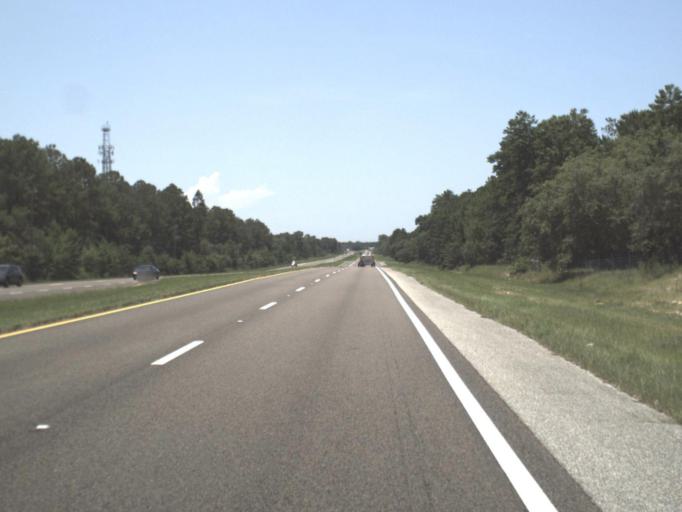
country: US
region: Florida
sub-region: Citrus County
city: Sugarmill Woods
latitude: 28.7143
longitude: -82.5376
